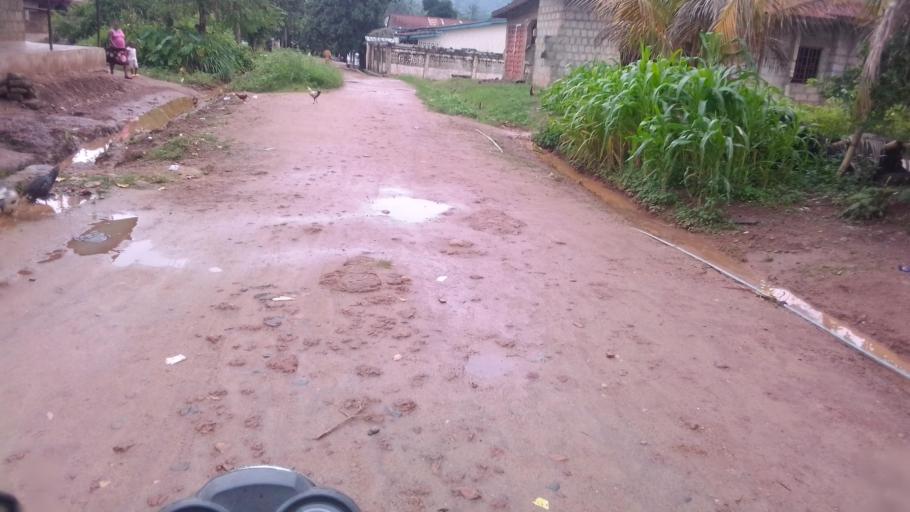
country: SL
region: Eastern Province
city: Kenema
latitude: 7.8877
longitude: -11.1840
